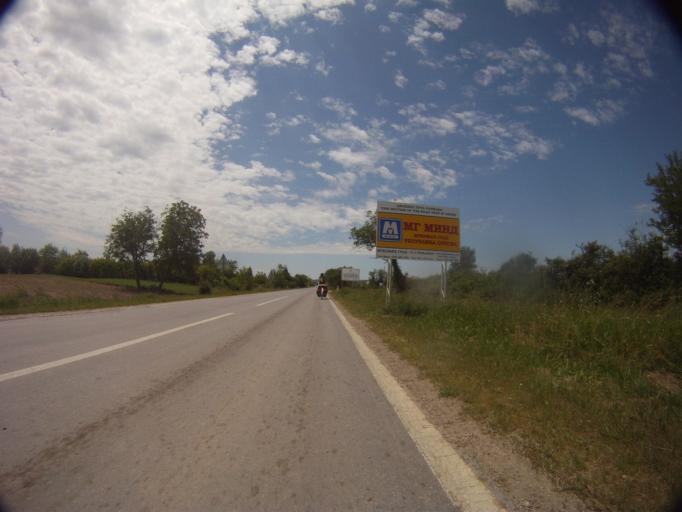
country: BA
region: Federation of Bosnia and Herzegovina
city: Odzak
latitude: 44.9938
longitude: 18.3127
